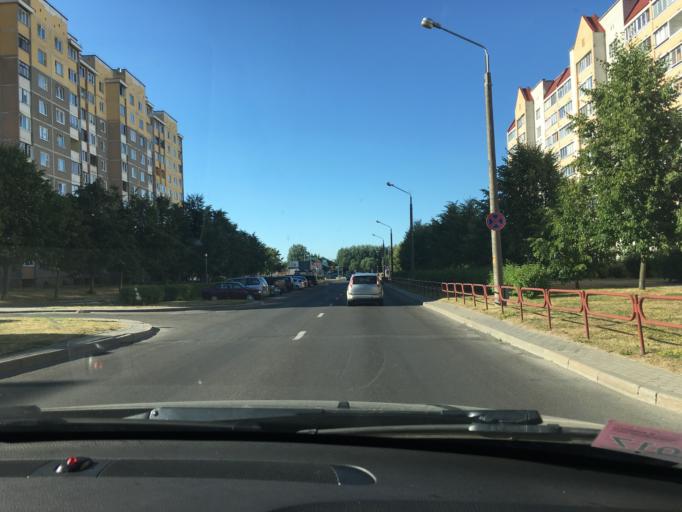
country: BY
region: Grodnenskaya
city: Hrodna
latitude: 53.7141
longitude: 23.8497
